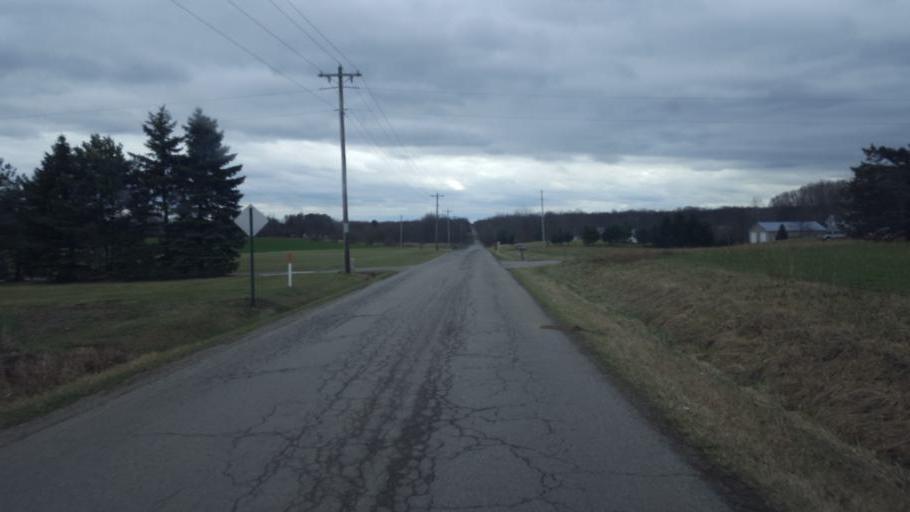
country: US
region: Ohio
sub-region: Knox County
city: Centerburg
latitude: 40.4335
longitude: -82.6854
